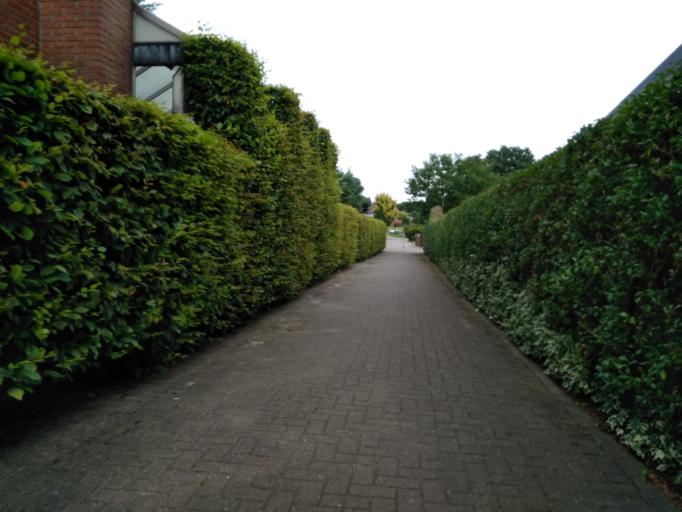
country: DE
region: North Rhine-Westphalia
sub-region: Regierungsbezirk Dusseldorf
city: Schermbeck
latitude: 51.6877
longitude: 6.8739
